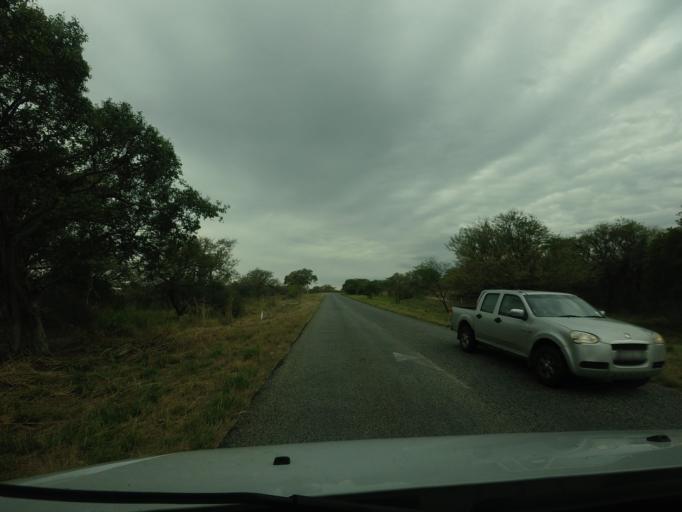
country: ZA
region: Limpopo
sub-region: Mopani District Municipality
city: Hoedspruit
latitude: -24.5067
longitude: 30.9223
